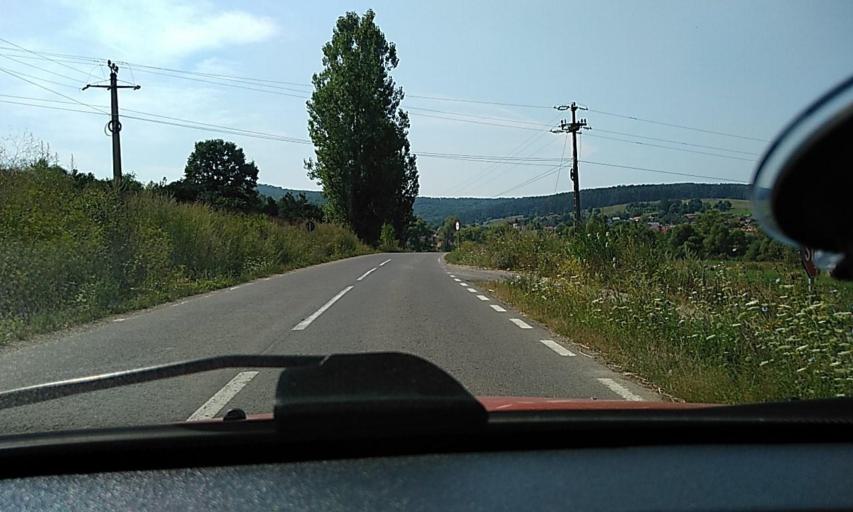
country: RO
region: Brasov
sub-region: Oras Rupea
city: Fiser
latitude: 46.0145
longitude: 25.1514
